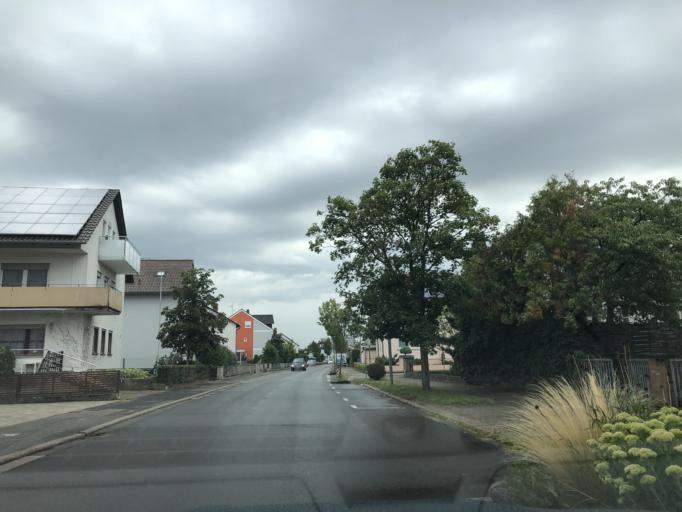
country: DE
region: Rheinland-Pfalz
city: Bellheim
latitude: 49.1979
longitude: 8.2880
